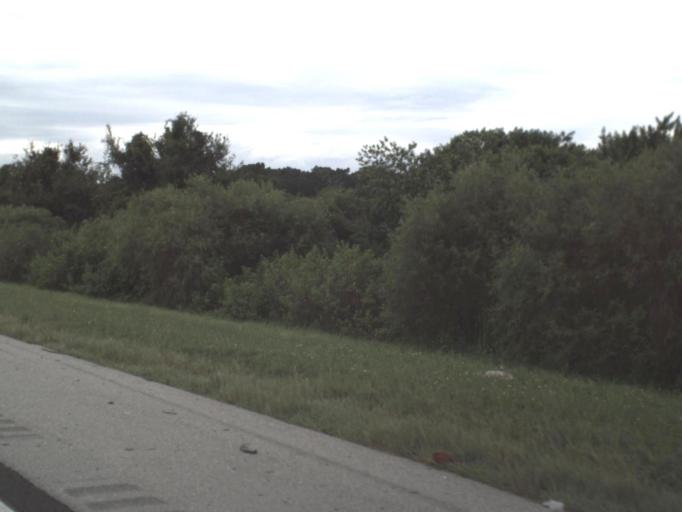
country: US
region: Florida
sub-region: Sarasota County
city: Lake Sarasota
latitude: 27.2889
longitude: -82.4487
